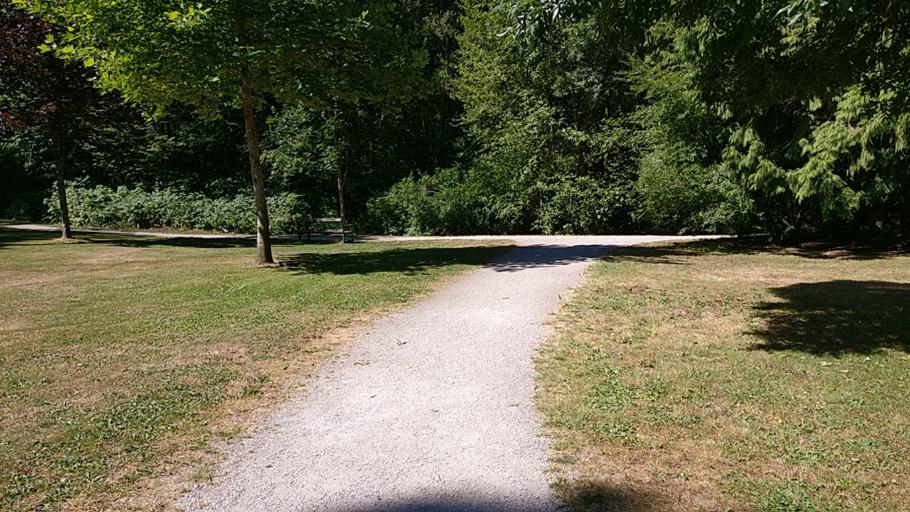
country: CA
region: British Columbia
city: Surrey
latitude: 49.0505
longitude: -122.8608
